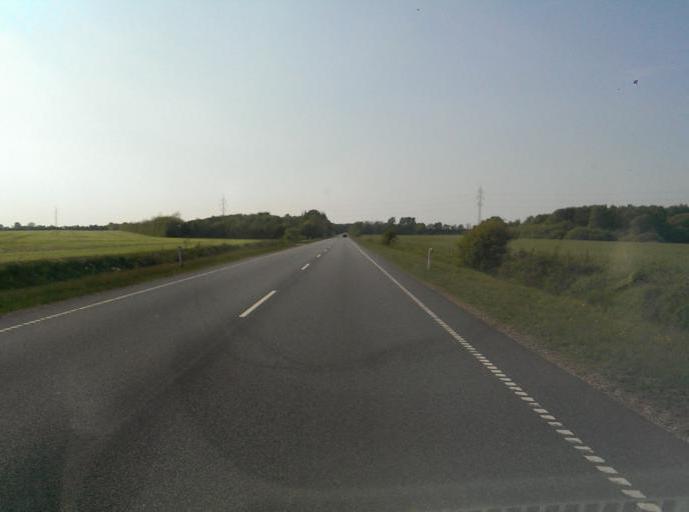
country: DK
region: South Denmark
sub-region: Esbjerg Kommune
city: Tjaereborg
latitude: 55.5015
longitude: 8.6096
